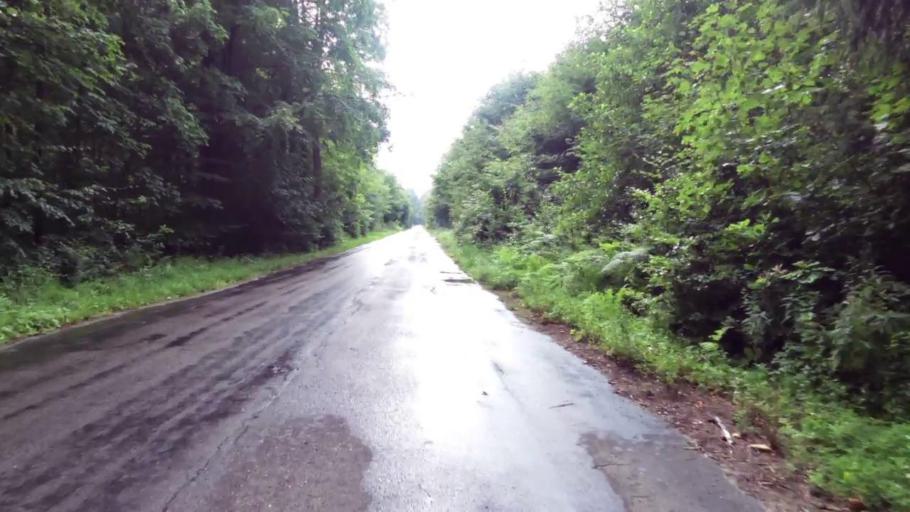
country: PL
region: West Pomeranian Voivodeship
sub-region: Powiat szczecinecki
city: Lubowo
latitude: 53.6013
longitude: 16.3112
